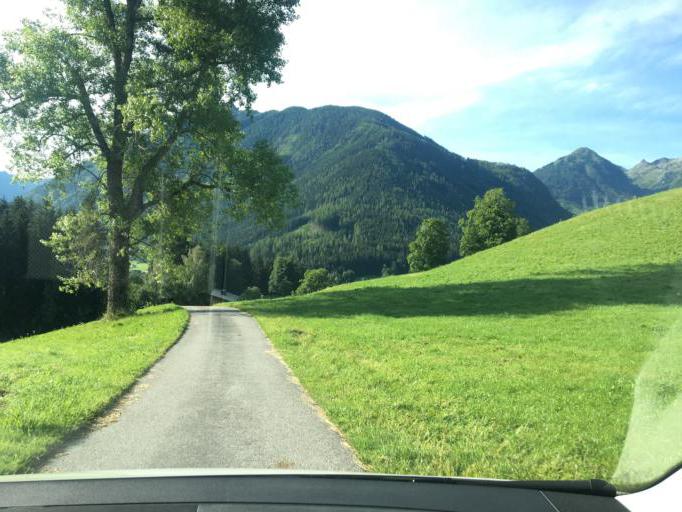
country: AT
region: Styria
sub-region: Politischer Bezirk Liezen
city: Schladming
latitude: 47.3756
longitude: 13.6696
